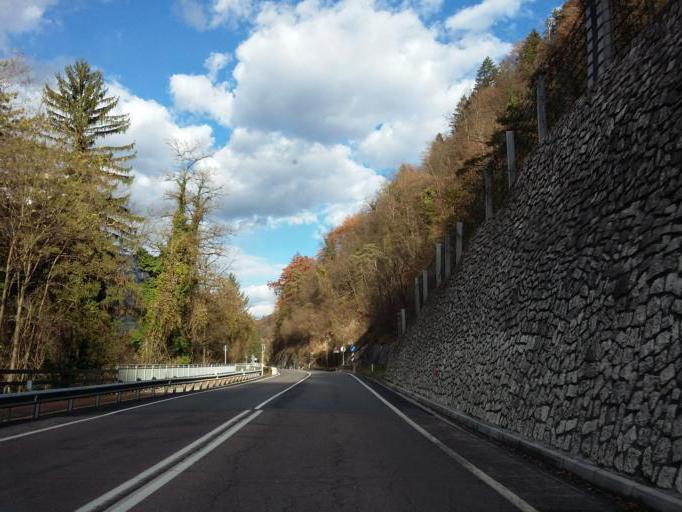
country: IT
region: Trentino-Alto Adige
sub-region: Provincia di Trento
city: Dorsino
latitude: 46.0474
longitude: 10.8987
